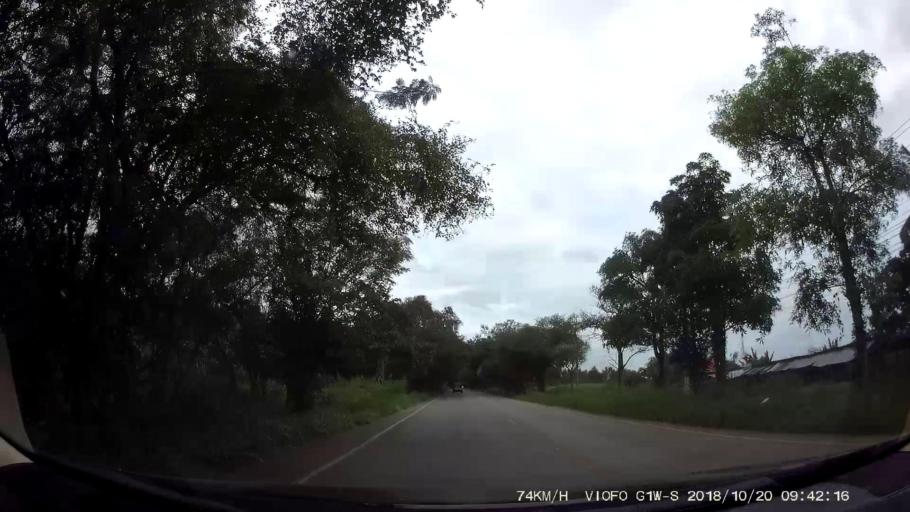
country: TH
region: Chaiyaphum
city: Khon San
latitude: 16.4621
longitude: 101.9531
